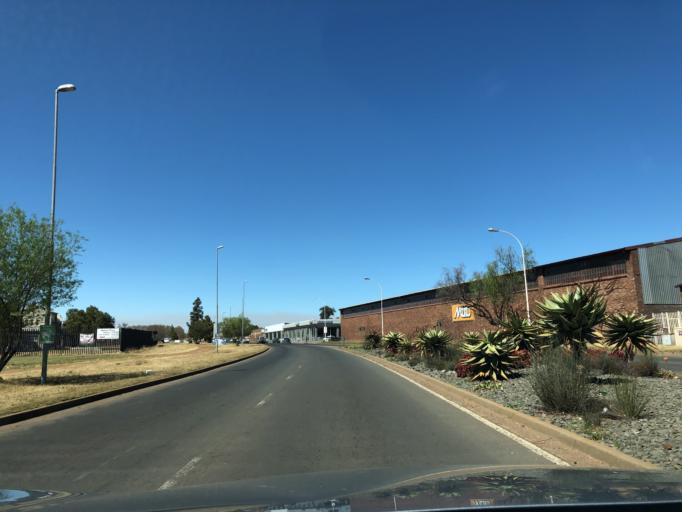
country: ZA
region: KwaZulu-Natal
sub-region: Amajuba District Municipality
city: Newcastle
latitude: -27.7514
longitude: 29.9381
